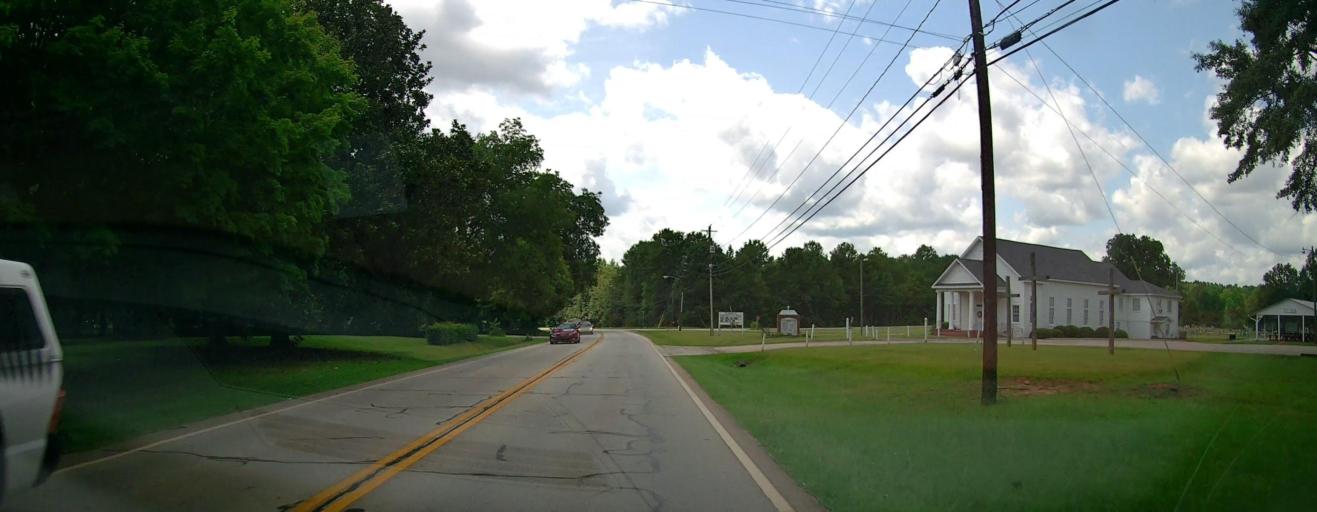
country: US
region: Georgia
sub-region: Troup County
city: Hogansville
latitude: 33.2318
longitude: -84.9485
